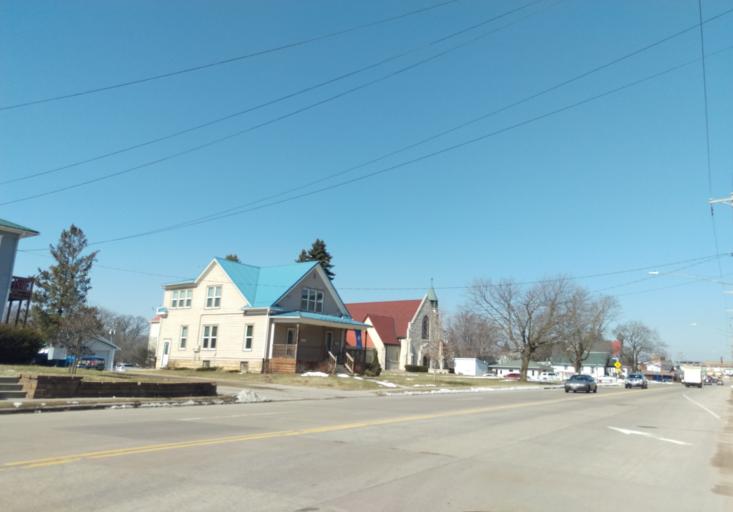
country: US
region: Wisconsin
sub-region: Vernon County
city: Viroqua
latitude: 43.5510
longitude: -90.8887
